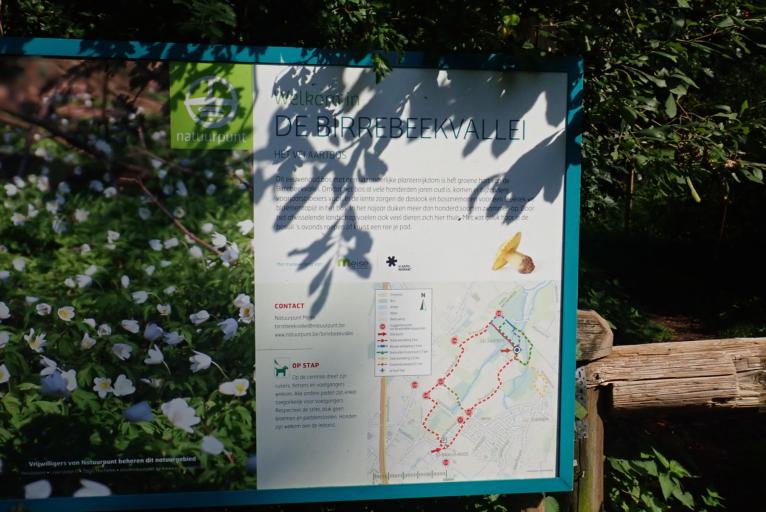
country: BE
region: Flanders
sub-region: Provincie Vlaams-Brabant
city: Meise
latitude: 50.9682
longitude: 4.3411
